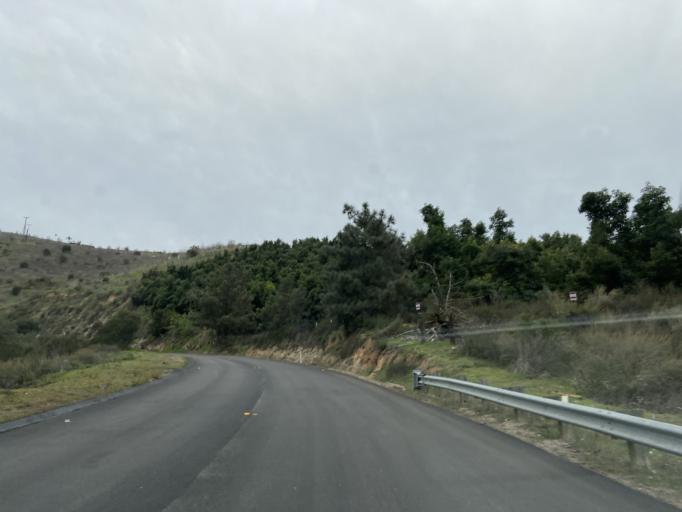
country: US
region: California
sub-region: San Diego County
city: Valley Center
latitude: 33.3073
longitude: -117.0191
